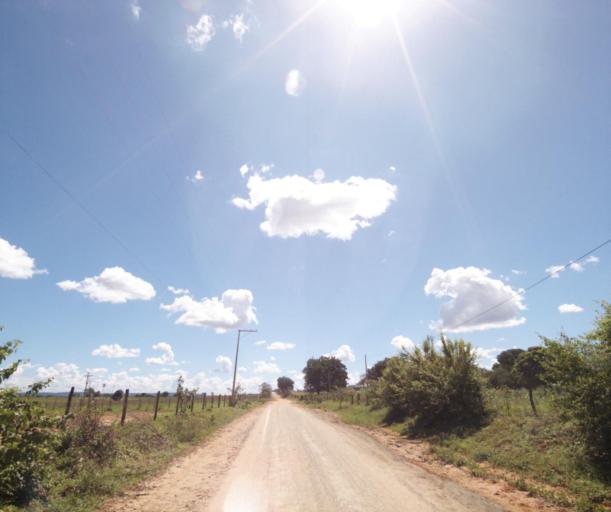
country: BR
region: Bahia
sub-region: Carinhanha
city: Carinhanha
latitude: -14.2171
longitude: -44.2871
